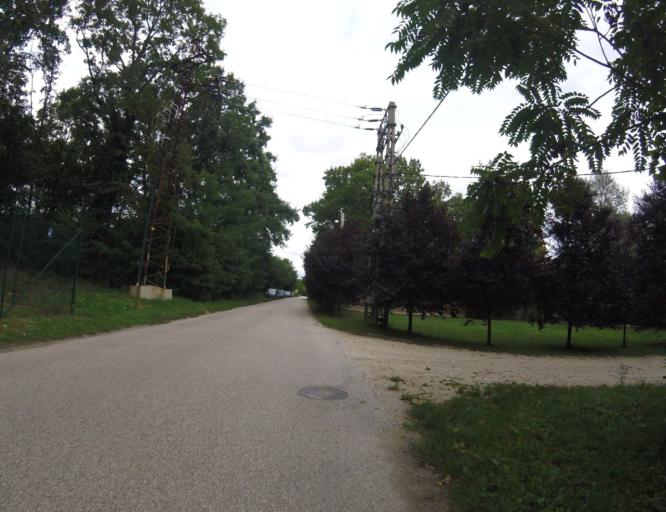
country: HU
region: Pest
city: Szigethalom
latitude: 47.2930
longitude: 19.0122
